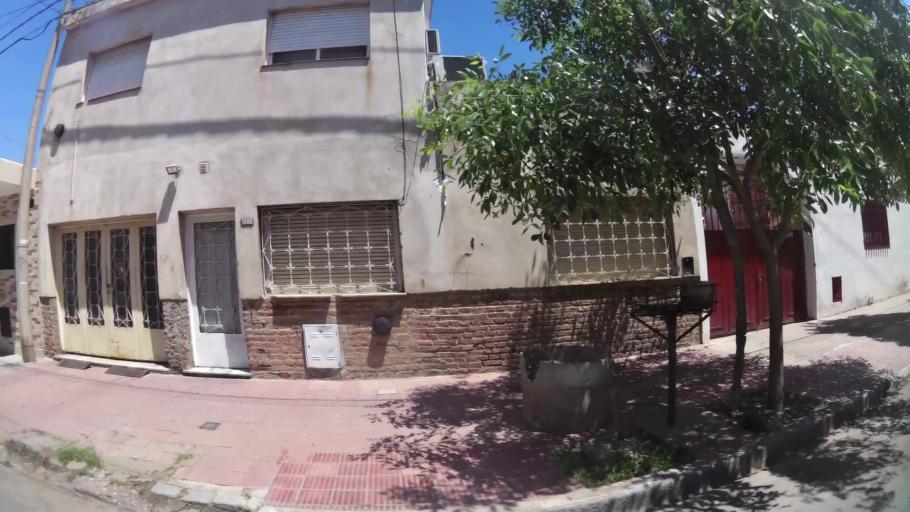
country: AR
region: Cordoba
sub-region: Departamento de Capital
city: Cordoba
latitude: -31.3826
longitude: -64.1470
